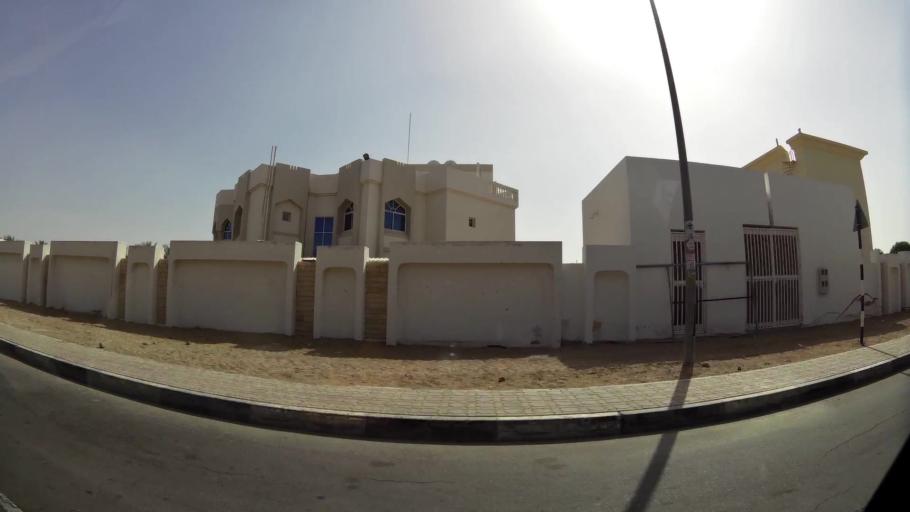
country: AE
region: Abu Dhabi
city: Al Ain
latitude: 24.2427
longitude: 55.6993
